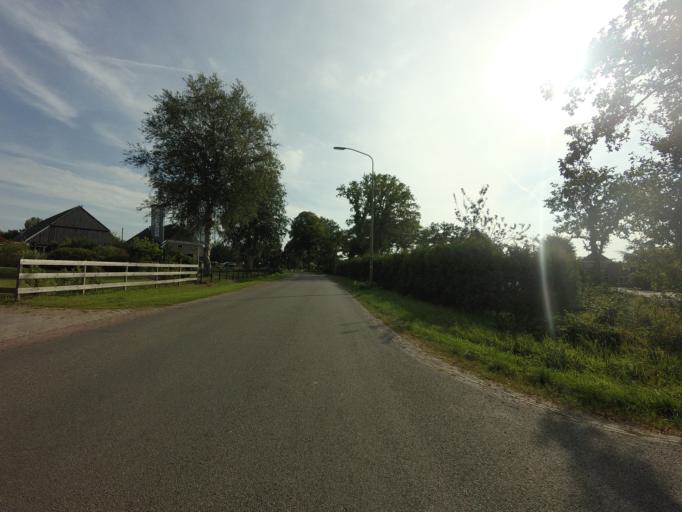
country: NL
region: Drenthe
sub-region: Gemeente Tynaarlo
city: Vries
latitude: 53.1288
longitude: 6.5666
